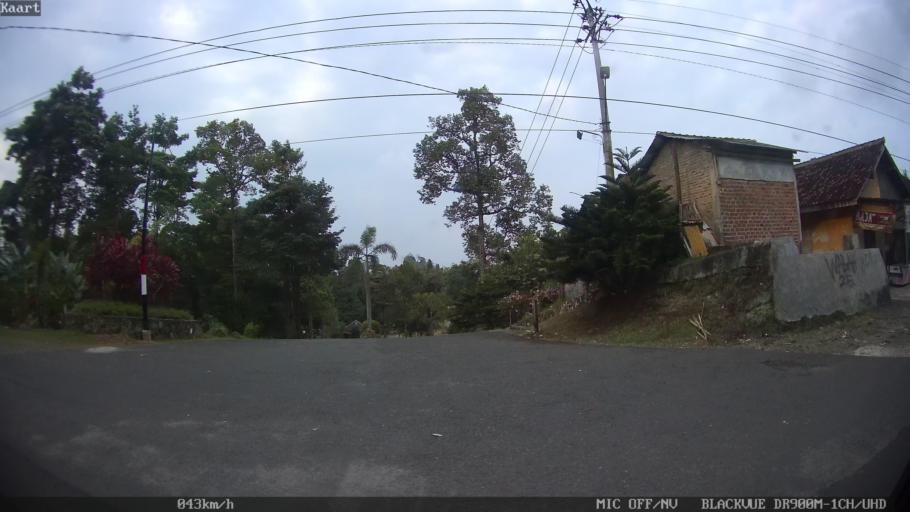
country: ID
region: Lampung
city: Bandarlampung
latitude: -5.4155
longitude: 105.2305
